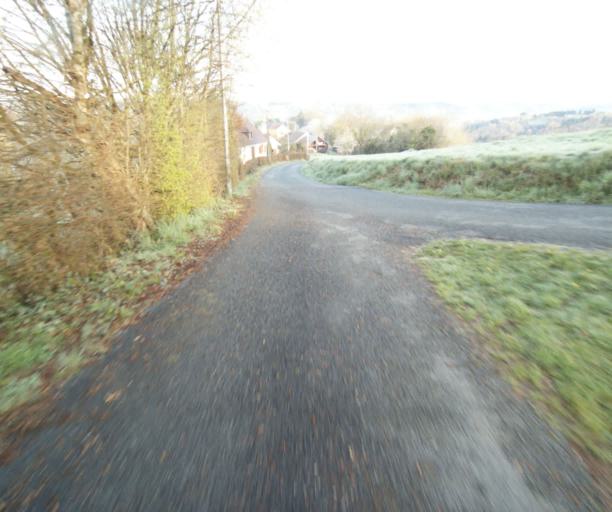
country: FR
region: Limousin
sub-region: Departement de la Correze
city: Naves
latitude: 45.3126
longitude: 1.8242
